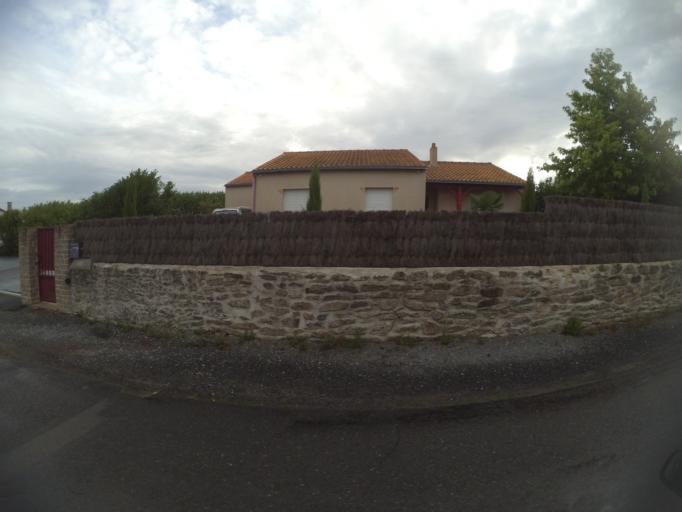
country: FR
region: Pays de la Loire
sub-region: Departement de la Loire-Atlantique
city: Aigrefeuille-sur-Maine
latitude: 47.0677
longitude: -1.4002
